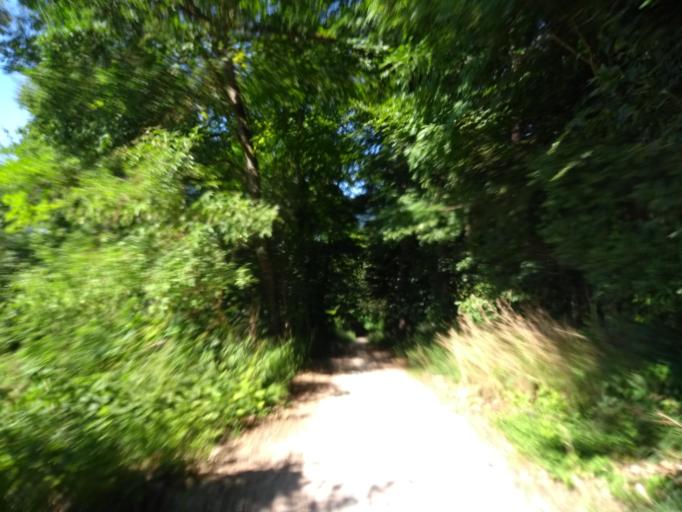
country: DE
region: Baden-Wuerttemberg
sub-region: Tuebingen Region
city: Ehingen
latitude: 48.2837
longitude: 9.6923
